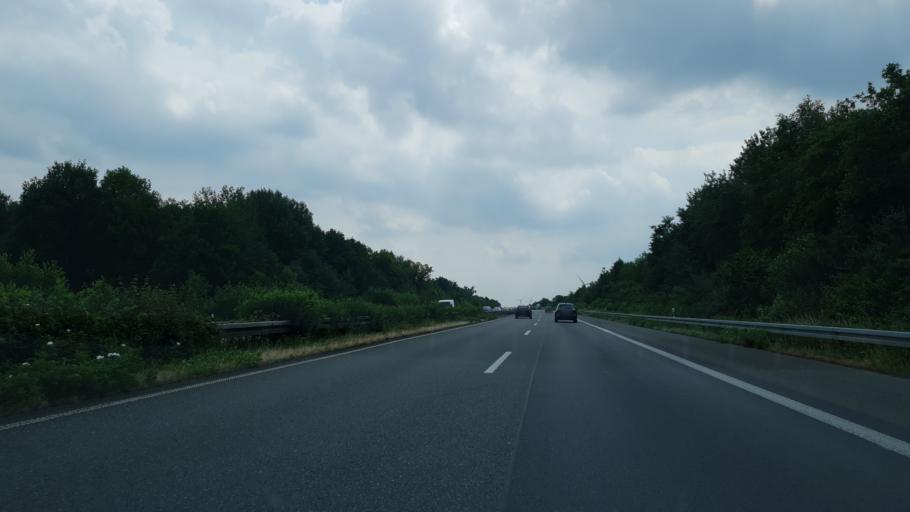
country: DE
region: North Rhine-Westphalia
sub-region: Regierungsbezirk Munster
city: Ochtrup
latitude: 52.2133
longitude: 7.1288
